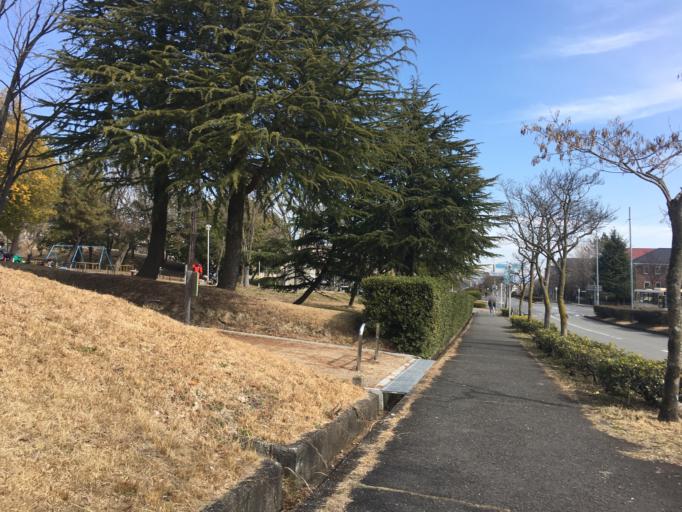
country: JP
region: Osaka
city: Mino
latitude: 34.8165
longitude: 135.5029
